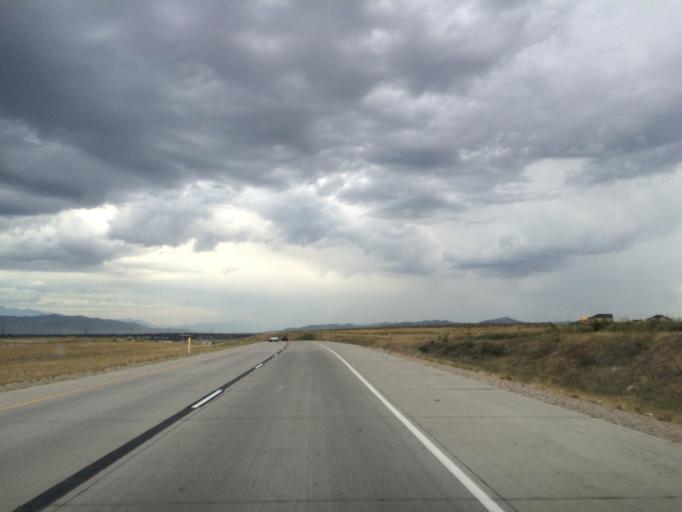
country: US
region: Utah
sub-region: Salt Lake County
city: Oquirrh
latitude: 40.6202
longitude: -112.0433
